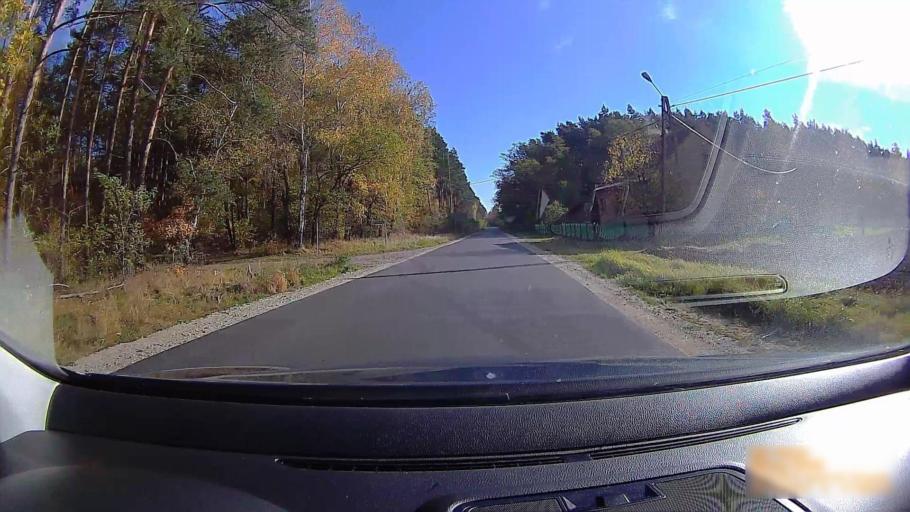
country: PL
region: Greater Poland Voivodeship
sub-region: Powiat ostrzeszowski
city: Ostrzeszow
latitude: 51.4107
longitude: 17.9930
